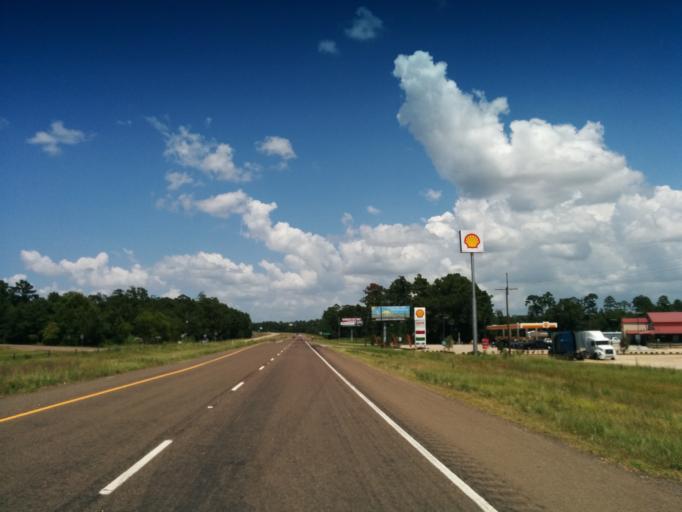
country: US
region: Texas
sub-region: Hardin County
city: Silsbee
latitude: 30.3247
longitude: -94.1682
